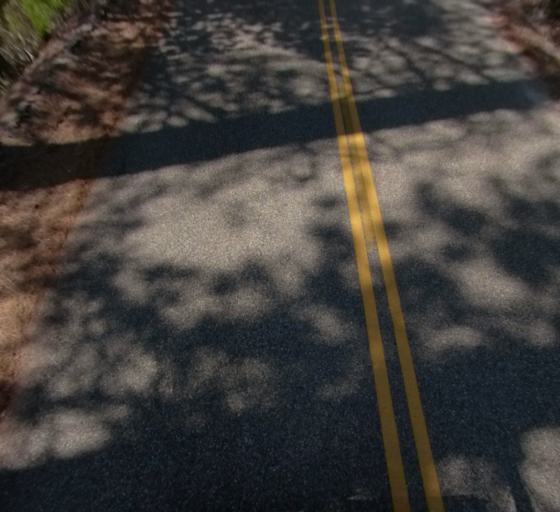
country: US
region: California
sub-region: Madera County
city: Oakhurst
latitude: 37.3509
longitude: -119.3860
